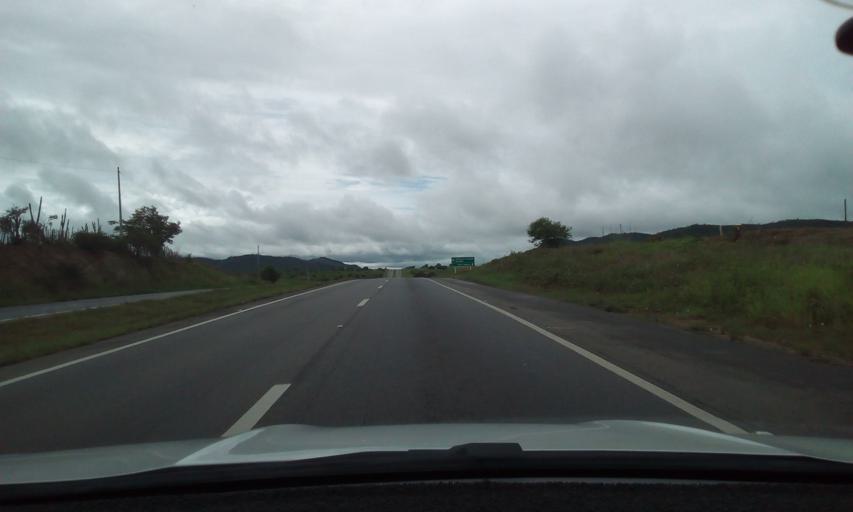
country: BR
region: Paraiba
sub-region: Gurinhem
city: Gurinhem
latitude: -7.1866
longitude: -35.4525
